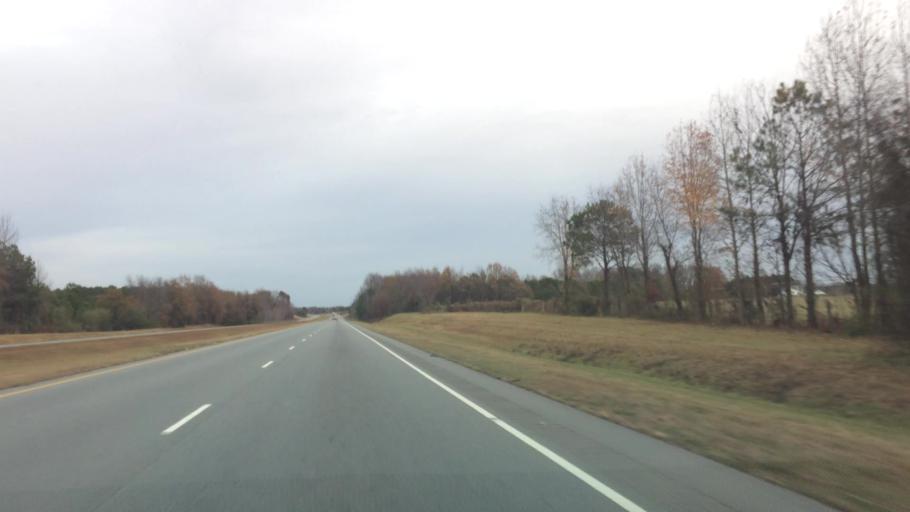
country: US
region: North Carolina
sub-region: Wayne County
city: Mount Olive
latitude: 35.1253
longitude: -78.1663
